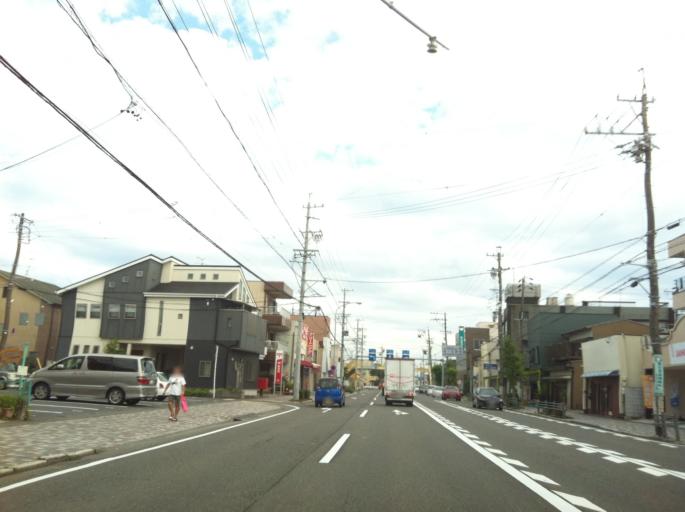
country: JP
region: Shizuoka
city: Shizuoka-shi
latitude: 35.0106
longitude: 138.4797
